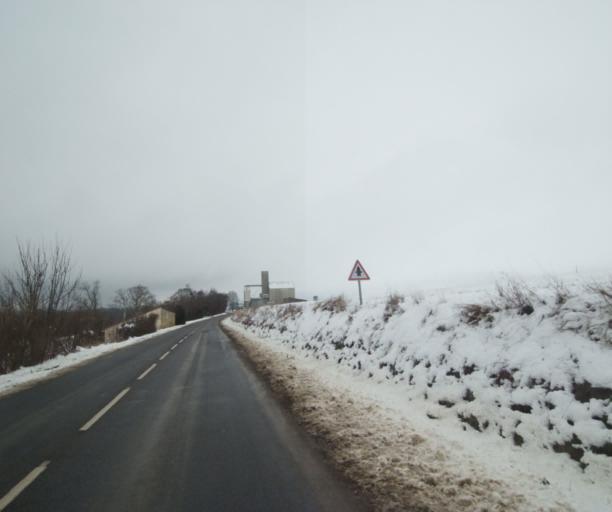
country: FR
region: Champagne-Ardenne
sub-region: Departement de la Haute-Marne
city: Wassy
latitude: 48.4309
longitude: 4.9623
